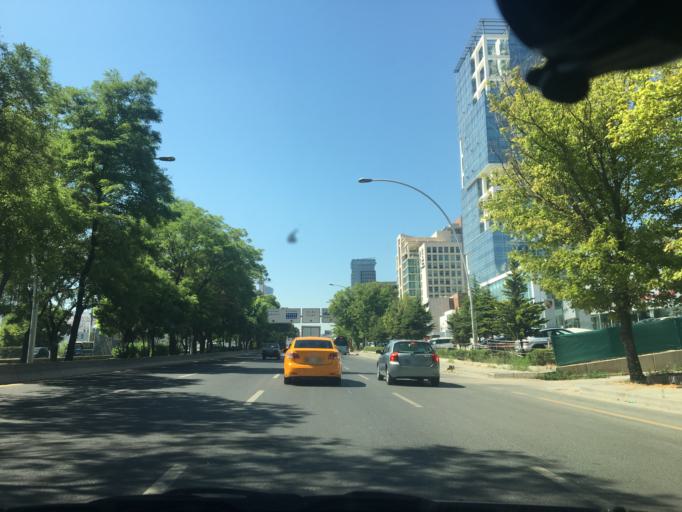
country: TR
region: Ankara
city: Ankara
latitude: 39.8925
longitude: 32.8128
